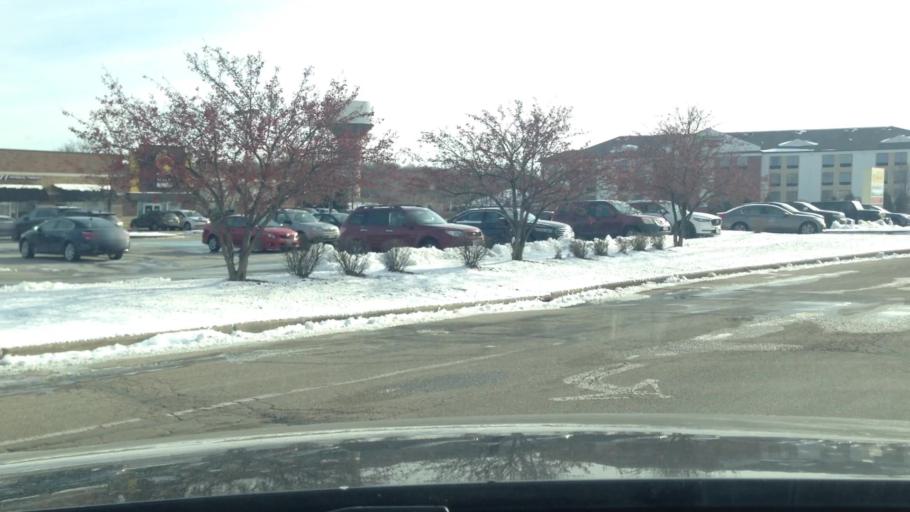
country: US
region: Wisconsin
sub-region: Waukesha County
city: New Berlin
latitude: 42.9570
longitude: -88.1067
